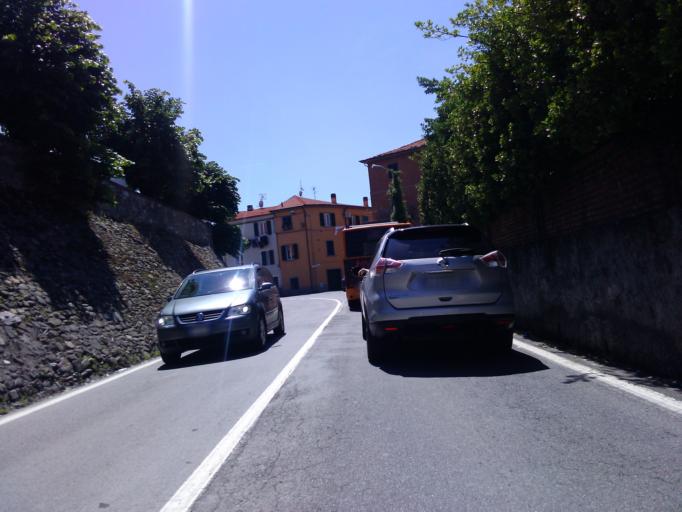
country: IT
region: Tuscany
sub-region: Provincia di Massa-Carrara
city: Albiano Magra
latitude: 44.1652
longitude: 9.9164
